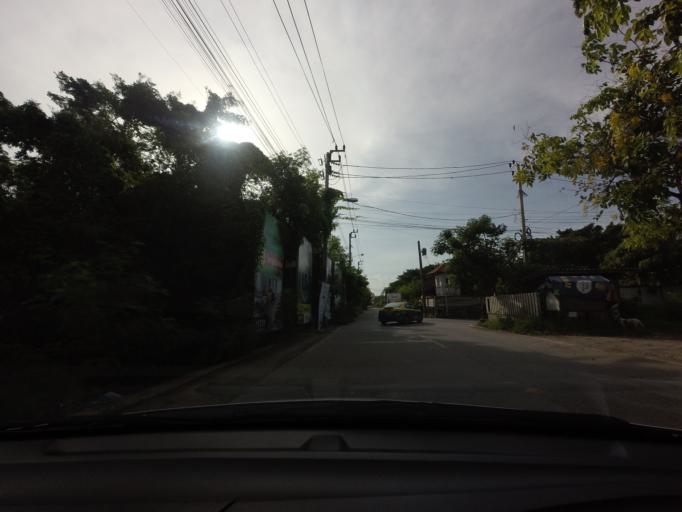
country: TH
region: Bangkok
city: Bang Na
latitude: 13.6508
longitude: 100.6558
